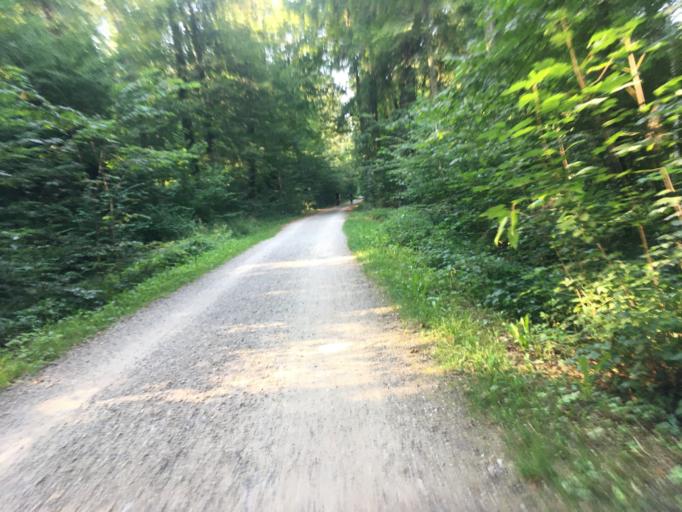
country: CH
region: Bern
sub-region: Emmental District
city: Oberburg
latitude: 47.0432
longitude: 7.6324
